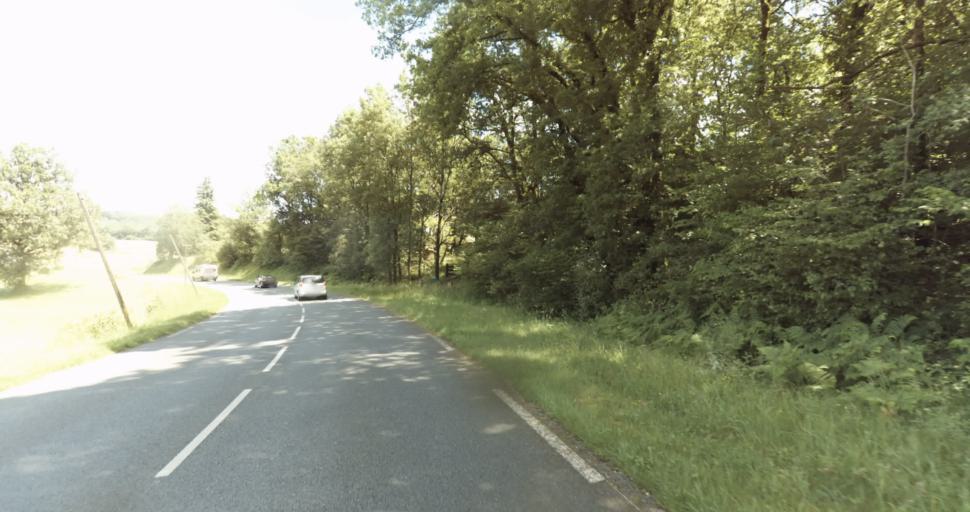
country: FR
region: Aquitaine
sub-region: Departement de la Dordogne
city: Beaumont-du-Perigord
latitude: 44.8441
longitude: 0.8332
